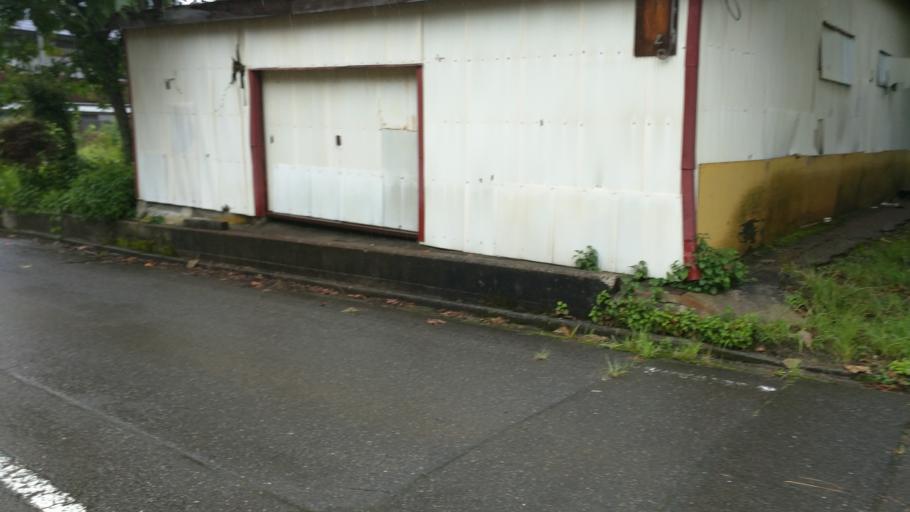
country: JP
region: Fukushima
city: Kitakata
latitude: 37.4699
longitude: 139.6530
